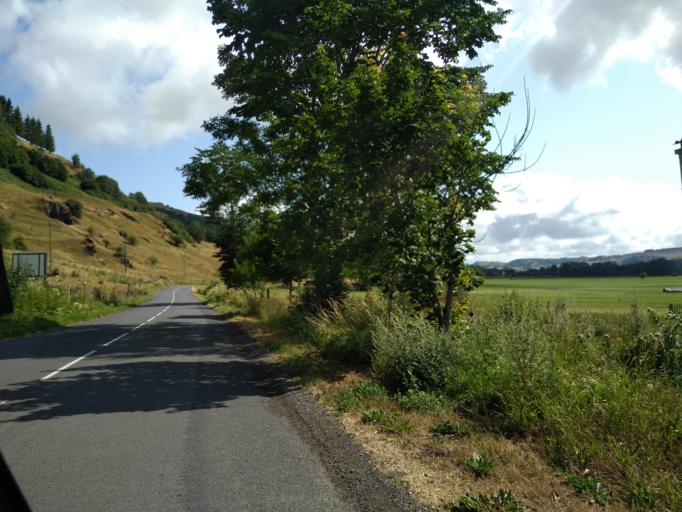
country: FR
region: Auvergne
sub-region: Departement du Cantal
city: Murat
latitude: 45.1520
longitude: 2.7770
